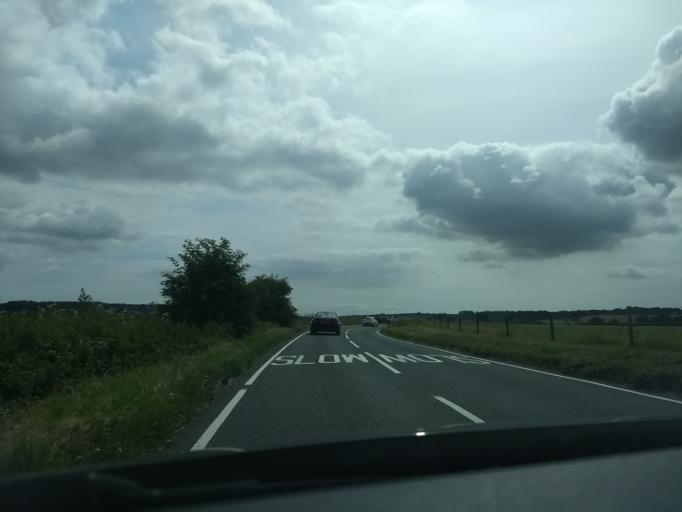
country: GB
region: England
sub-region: Suffolk
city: Ipswich
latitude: 52.0260
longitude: 1.1599
